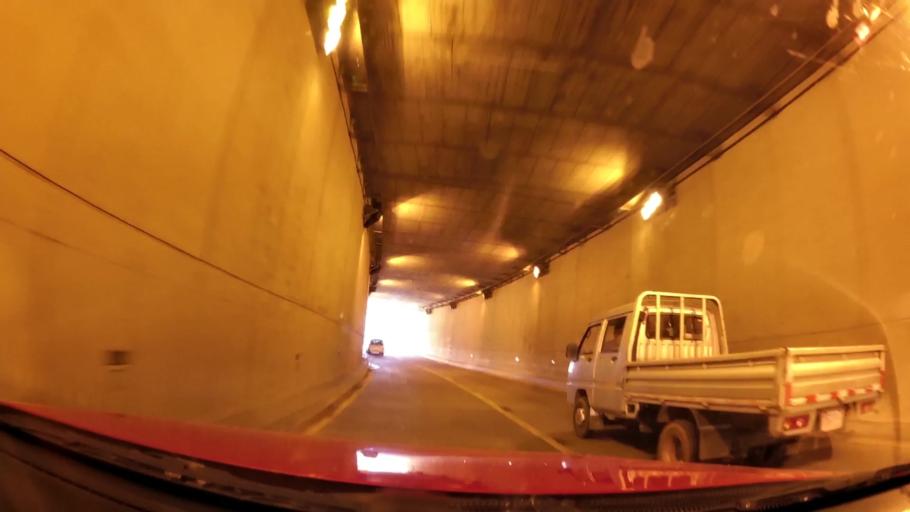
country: PY
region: Central
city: Colonia Mariano Roque Alonso
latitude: -25.2469
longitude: -57.5497
